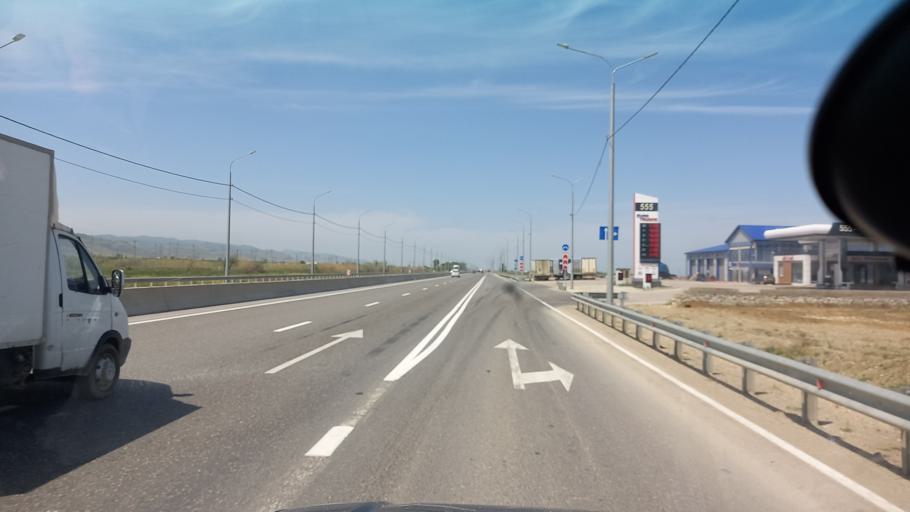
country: RU
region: Dagestan
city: Manas
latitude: 42.7416
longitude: 47.6593
